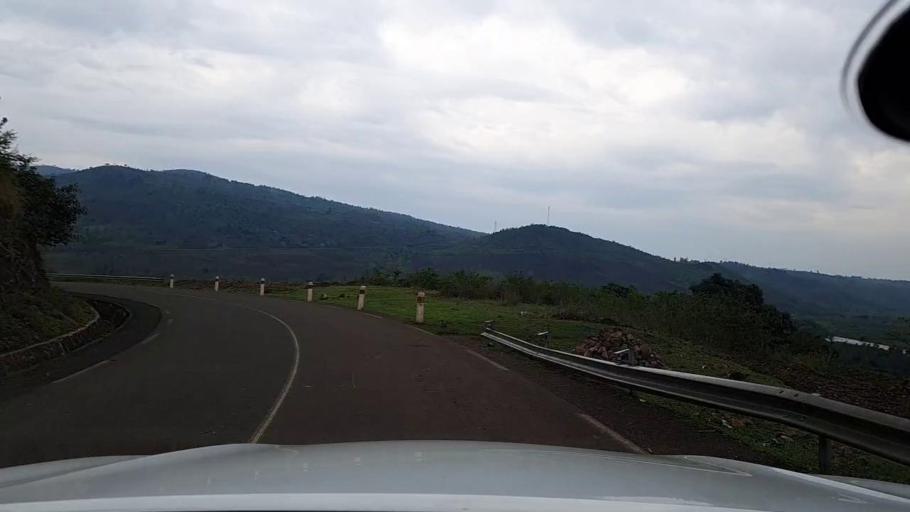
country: BI
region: Cibitoke
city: Cibitoke
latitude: -2.7352
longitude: 29.0363
